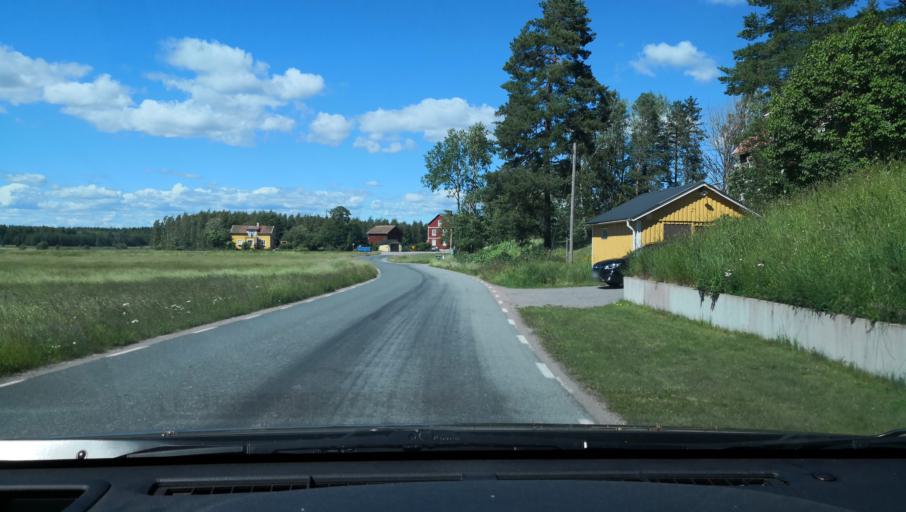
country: SE
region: Soedermanland
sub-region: Eskilstuna Kommun
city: Hallbybrunn
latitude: 59.3178
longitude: 16.3766
